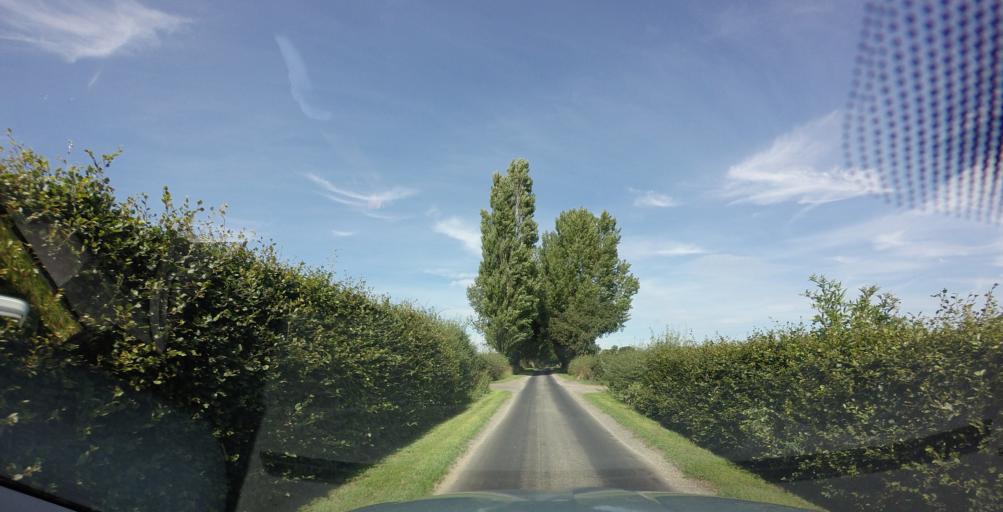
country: GB
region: England
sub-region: North Yorkshire
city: Ripon
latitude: 54.1107
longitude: -1.4758
